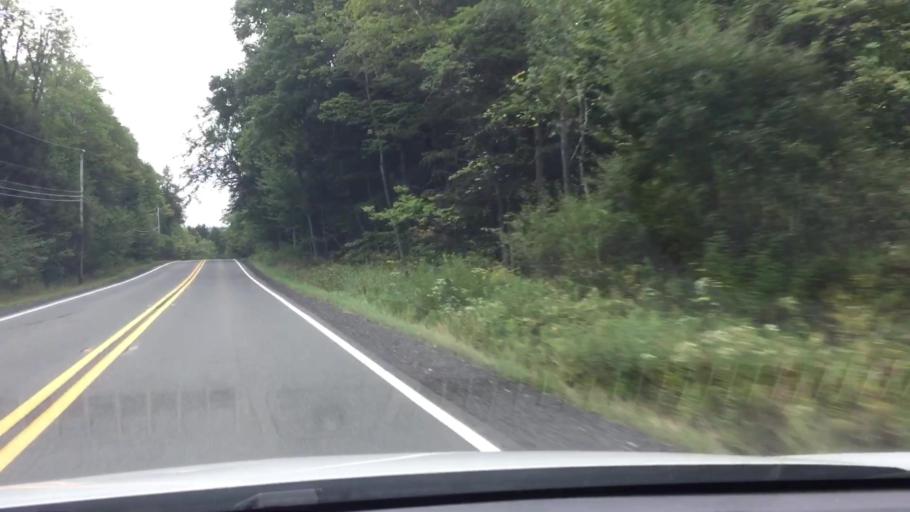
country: US
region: Massachusetts
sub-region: Berkshire County
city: Becket
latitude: 42.3436
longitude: -73.0916
